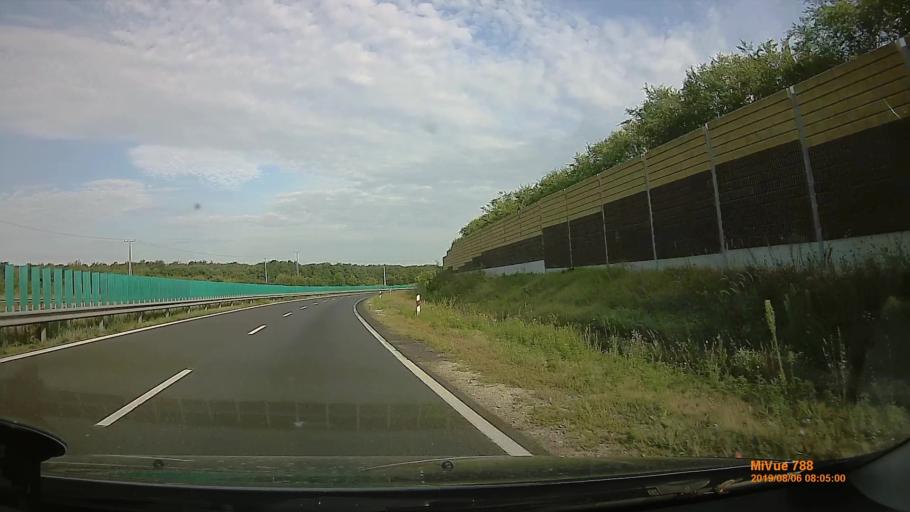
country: HU
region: Fejer
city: Szabadbattyan
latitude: 47.1502
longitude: 18.3876
